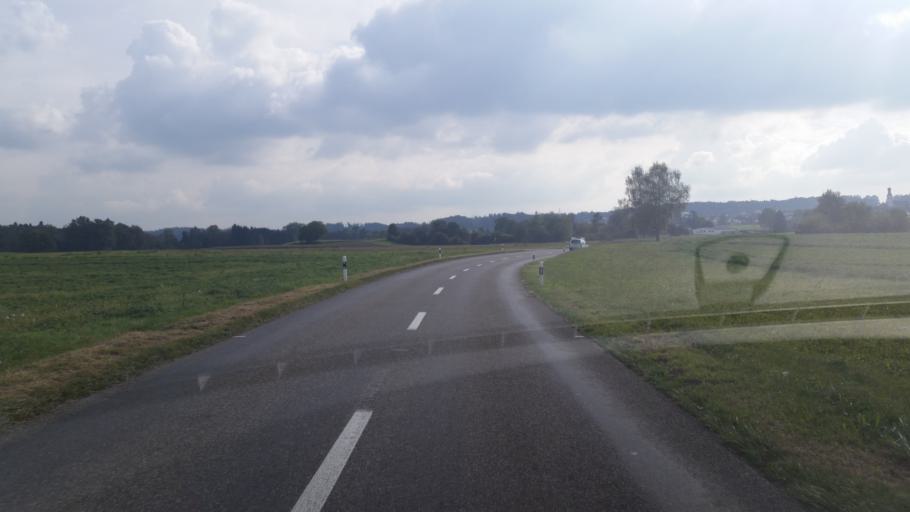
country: CH
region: Aargau
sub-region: Bezirk Baden
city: Kunten
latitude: 47.3873
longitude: 8.3024
